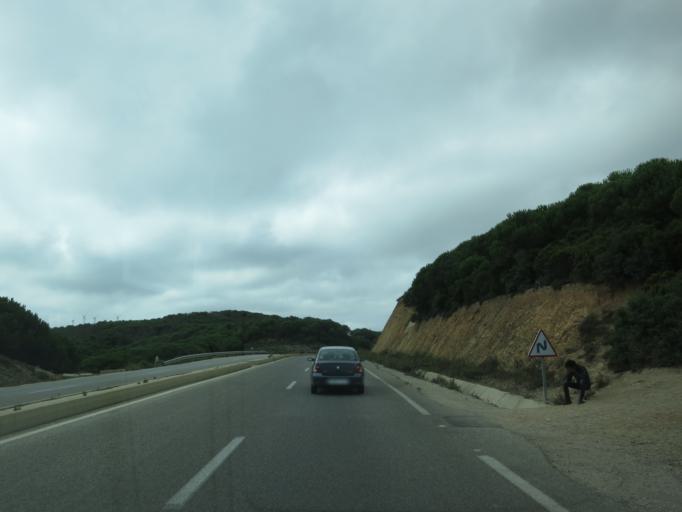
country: ES
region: Ceuta
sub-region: Ceuta
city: Ceuta
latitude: 35.8630
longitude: -5.4137
